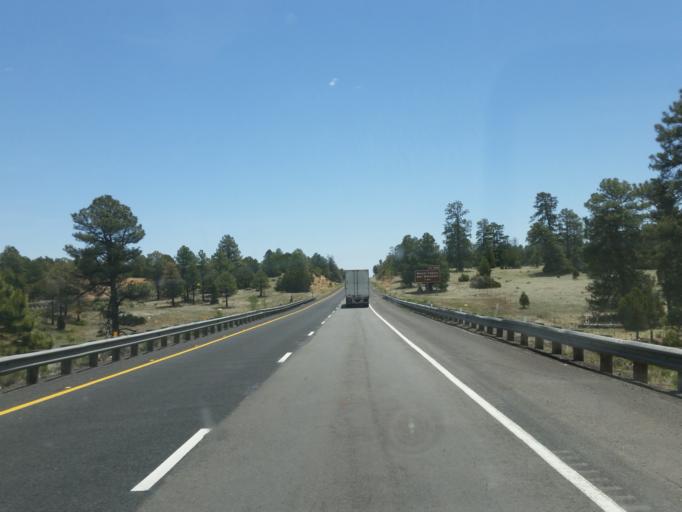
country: US
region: Arizona
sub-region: Coconino County
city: Flagstaff
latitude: 35.2143
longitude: -111.5429
